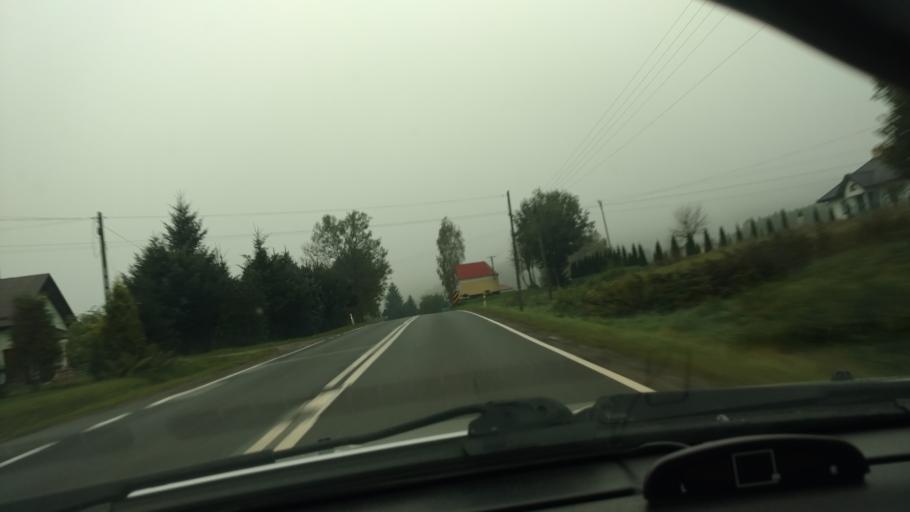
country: PL
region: Subcarpathian Voivodeship
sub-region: Powiat strzyzowski
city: Frysztak
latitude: 49.8625
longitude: 21.6265
